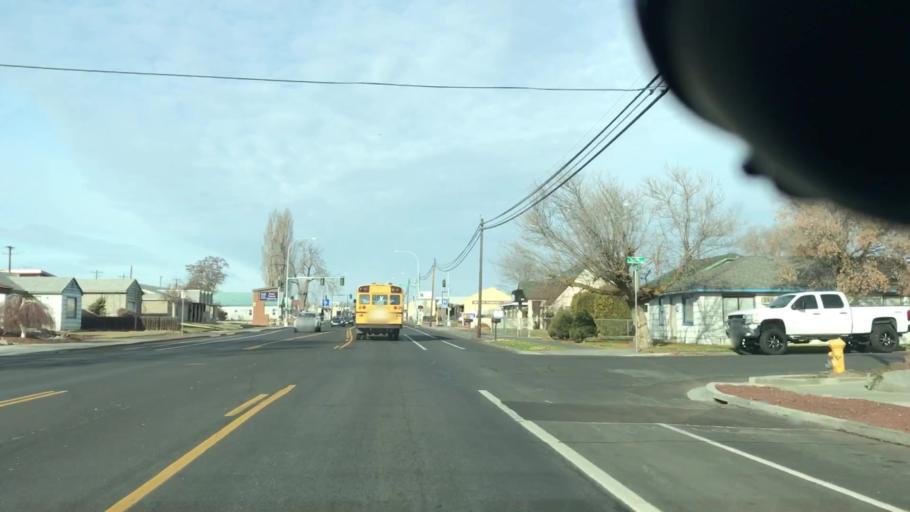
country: US
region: Washington
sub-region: Grant County
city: Moses Lake
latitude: 47.1276
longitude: -119.2753
